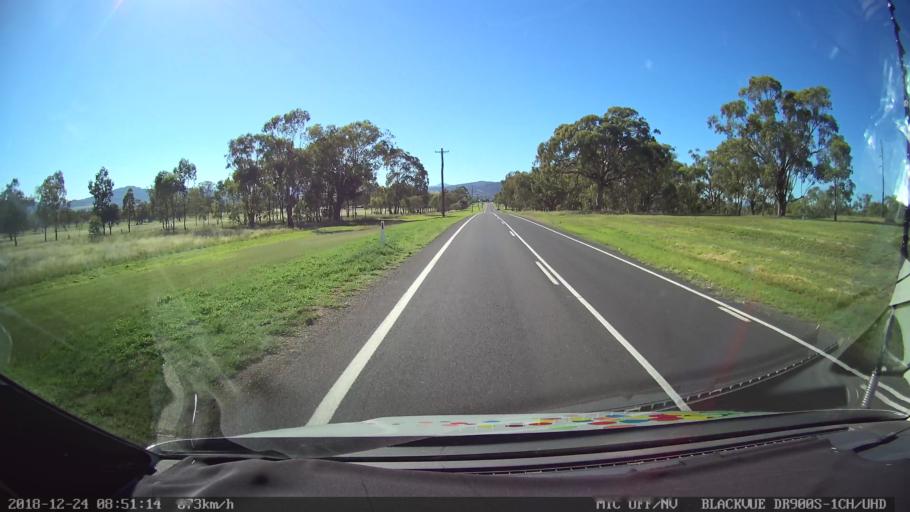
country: AU
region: New South Wales
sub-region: Liverpool Plains
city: Quirindi
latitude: -31.4826
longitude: 150.6725
